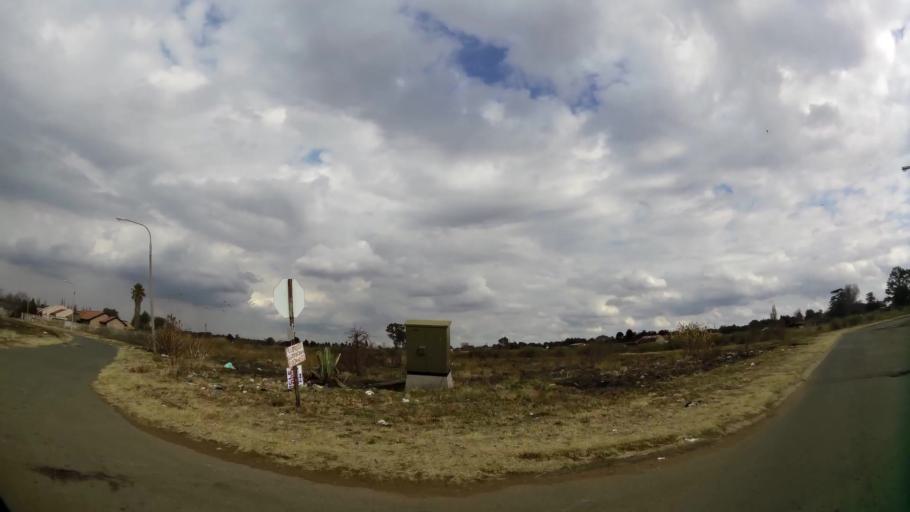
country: ZA
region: Gauteng
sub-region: Sedibeng District Municipality
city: Vanderbijlpark
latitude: -26.7083
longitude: 27.8010
